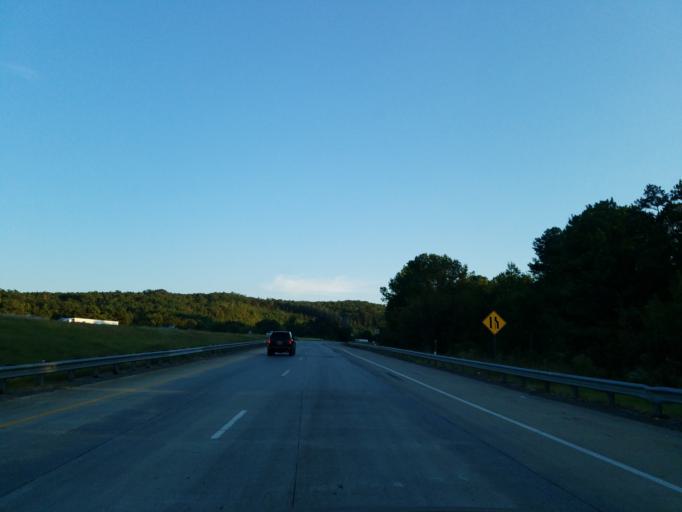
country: US
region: Georgia
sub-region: Bartow County
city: Cartersville
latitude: 34.2034
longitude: -84.7625
